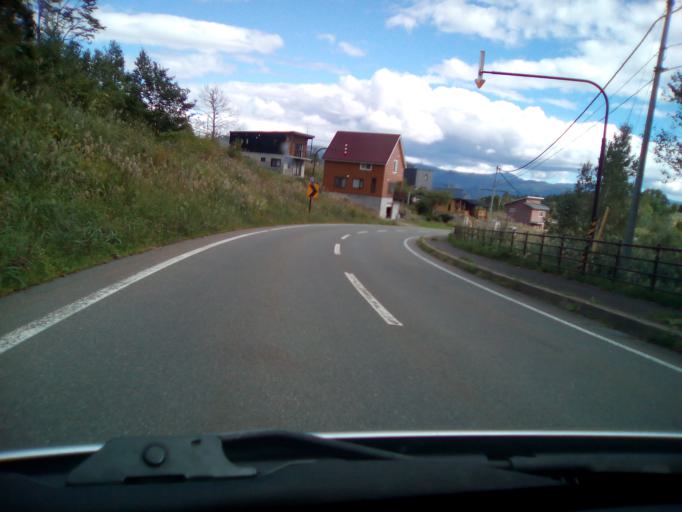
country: JP
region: Hokkaido
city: Date
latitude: 42.6478
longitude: 140.8115
